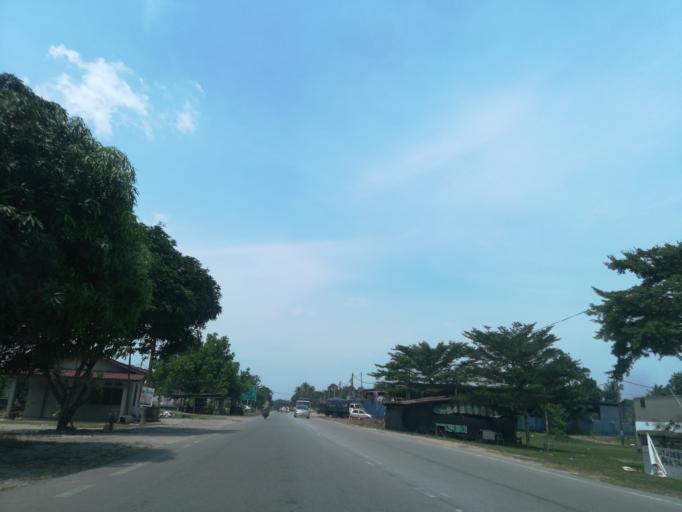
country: MY
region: Penang
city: Tasek Glugor
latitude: 5.4433
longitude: 100.5524
